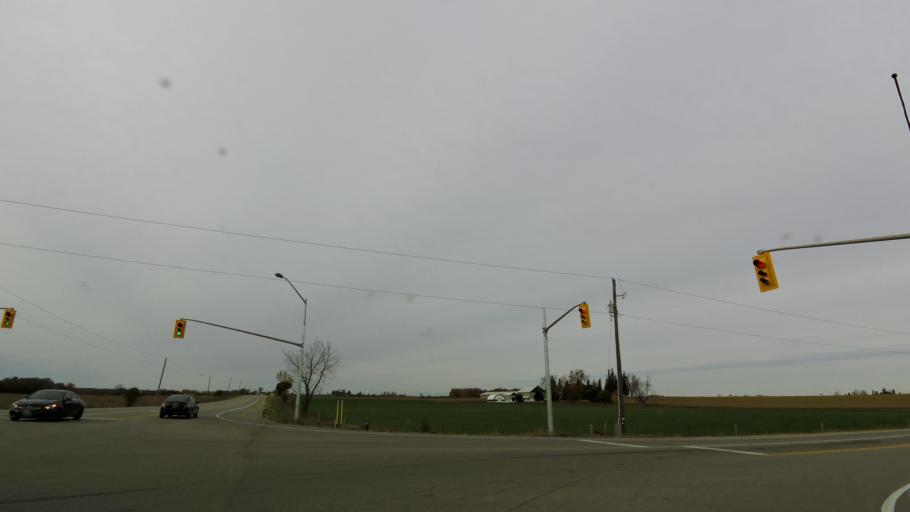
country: CA
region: Ontario
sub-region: Wellington County
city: Guelph
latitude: 43.5077
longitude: -80.3081
